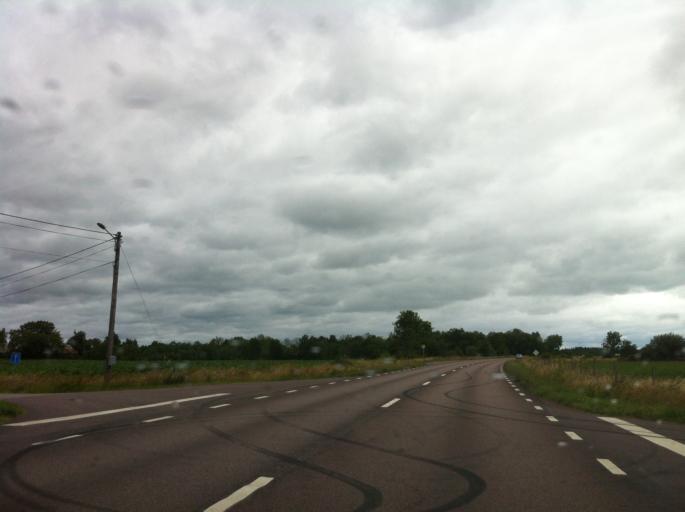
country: SE
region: Kalmar
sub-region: Borgholms Kommun
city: Borgholm
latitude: 57.1296
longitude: 16.9723
